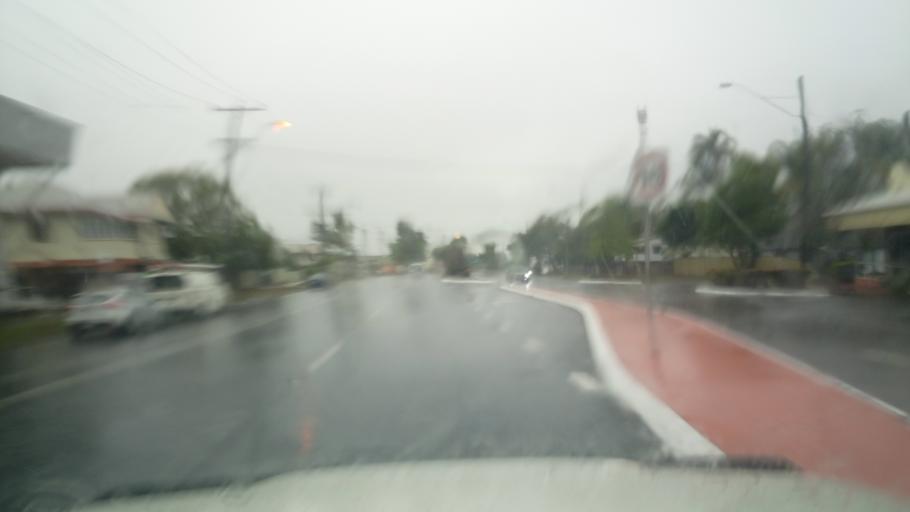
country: AU
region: Queensland
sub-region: Cairns
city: Cairns
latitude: -16.9357
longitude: 145.7630
